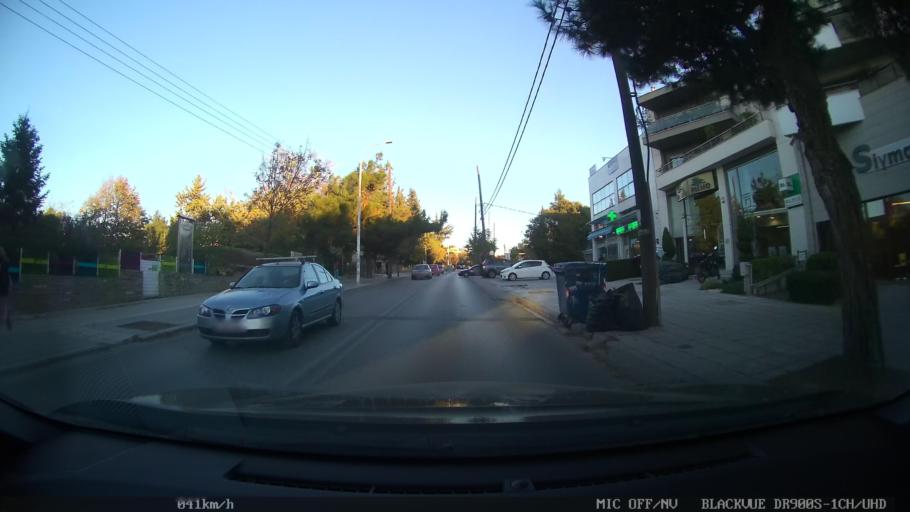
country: GR
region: Central Macedonia
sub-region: Nomos Thessalonikis
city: Pylaia
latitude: 40.6024
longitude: 22.9780
